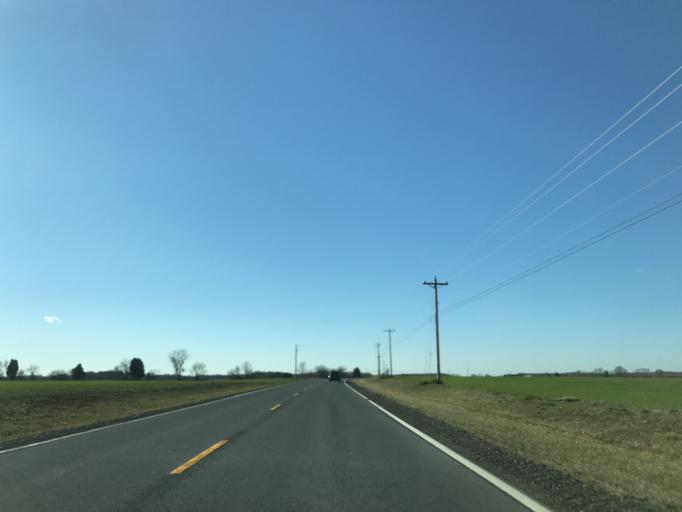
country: US
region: Maryland
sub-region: Queen Anne's County
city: Centreville
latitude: 39.0094
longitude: -75.9897
